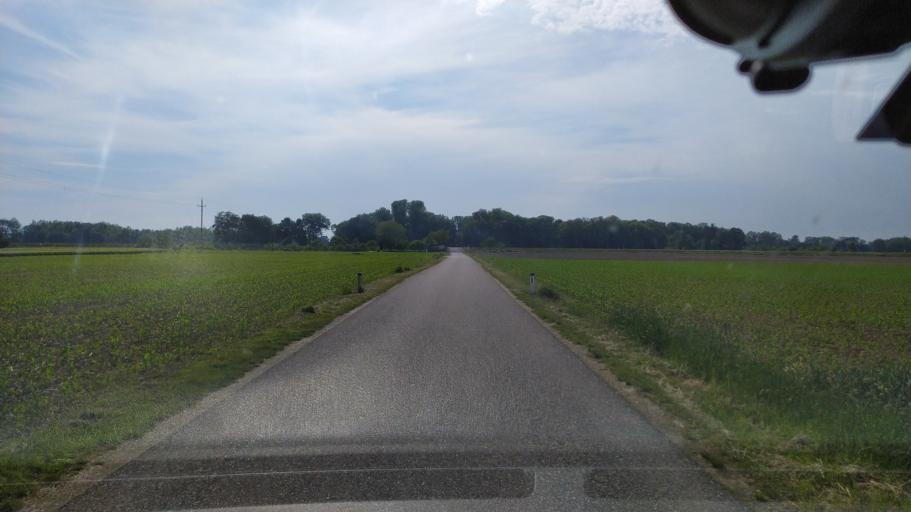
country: AT
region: Upper Austria
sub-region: Politischer Bezirk Perg
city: Bad Kreuzen
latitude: 48.1958
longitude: 14.7496
